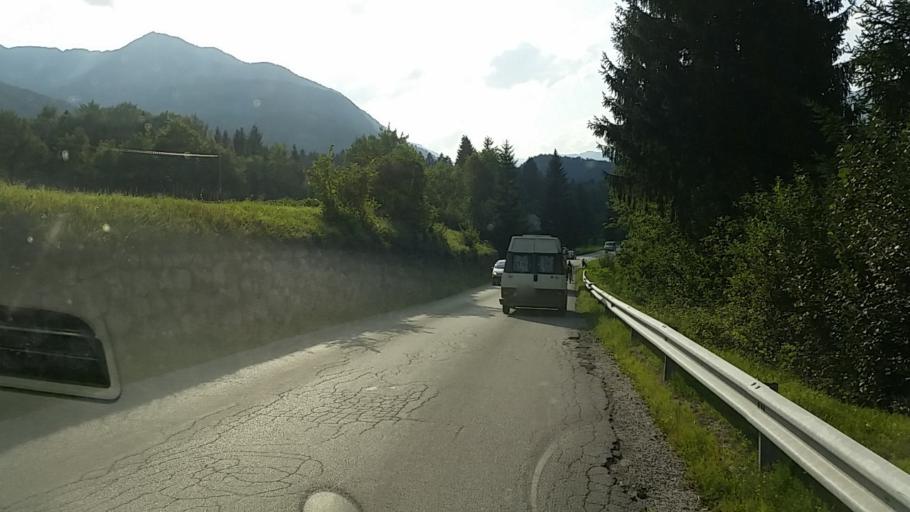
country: SI
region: Bohinj
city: Bohinjska Bistrica
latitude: 46.2682
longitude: 13.9004
